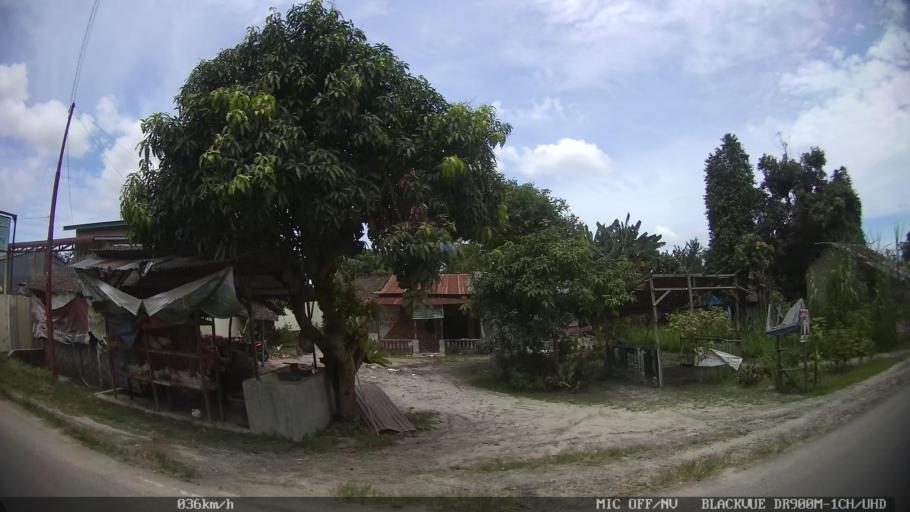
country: ID
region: North Sumatra
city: Percut
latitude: 3.5749
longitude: 98.8832
